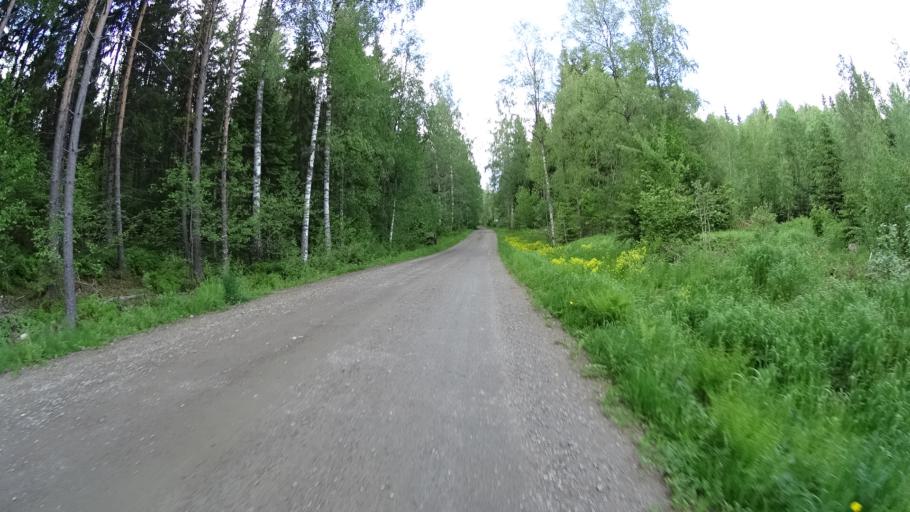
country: FI
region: Uusimaa
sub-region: Raaseporin
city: Pohja
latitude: 60.1679
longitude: 23.6005
